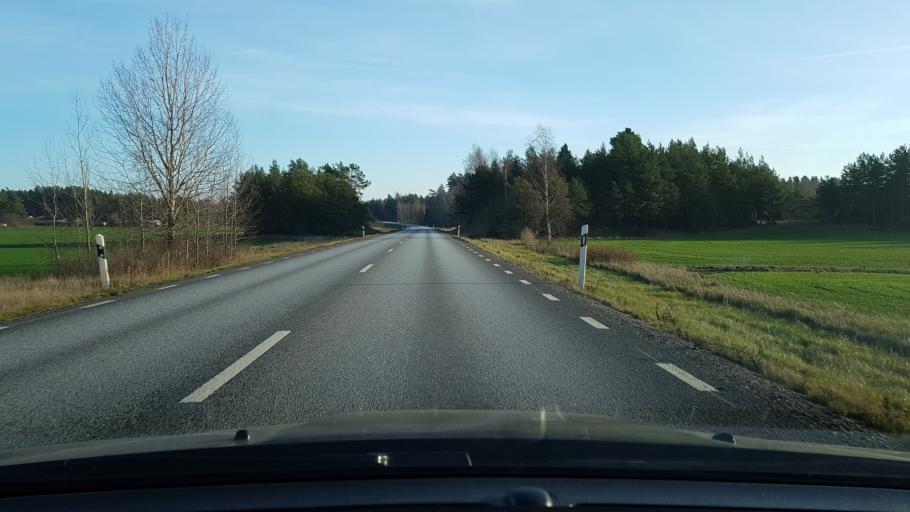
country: SE
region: Stockholm
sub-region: Vallentuna Kommun
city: Vallentuna
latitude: 59.7480
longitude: 18.0735
